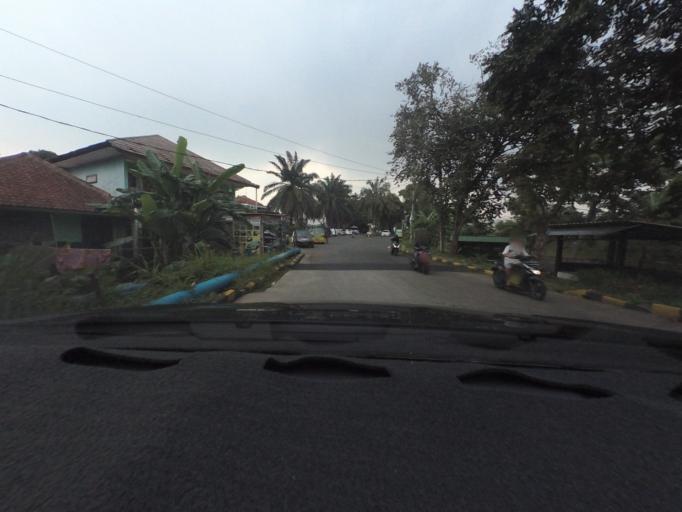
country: ID
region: West Java
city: Bogor
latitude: -6.5973
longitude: 106.8196
